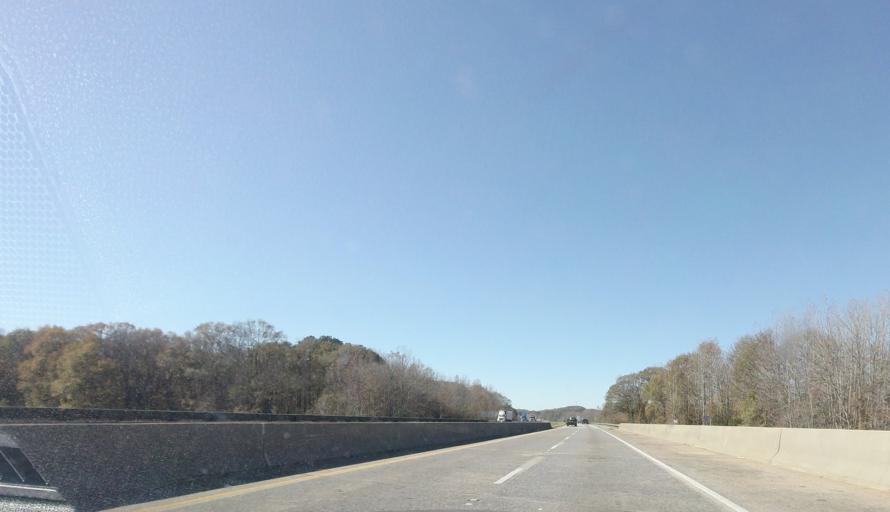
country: US
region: Alabama
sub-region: Calhoun County
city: Choccolocco
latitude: 33.6171
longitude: -85.7327
